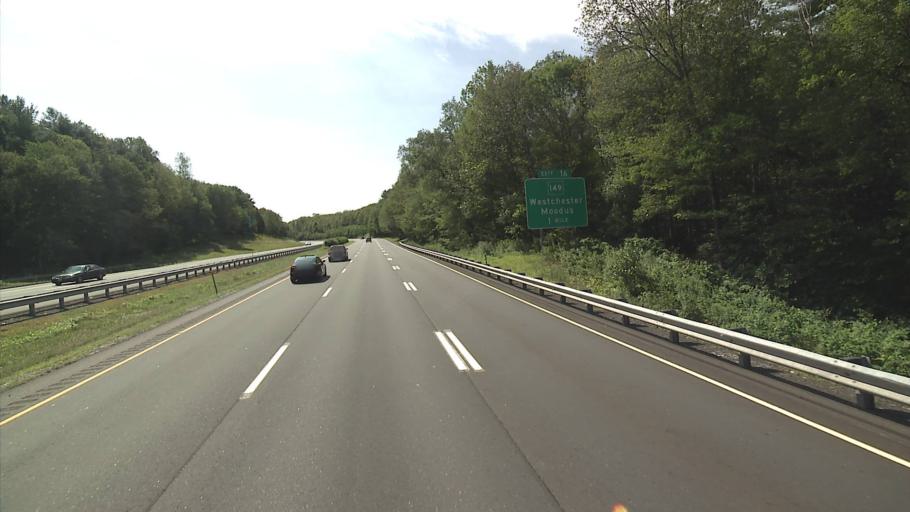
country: US
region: Connecticut
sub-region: Hartford County
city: Terramuggus
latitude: 41.5953
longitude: -72.4163
